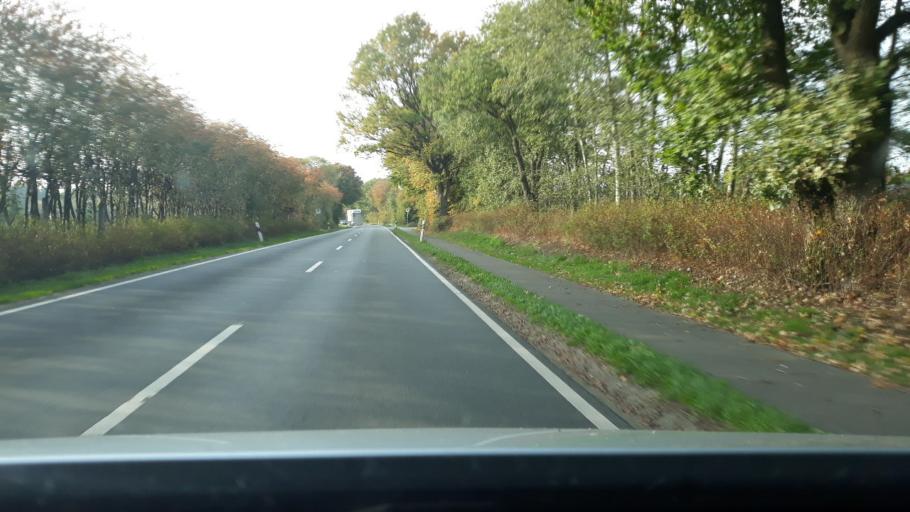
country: DE
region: Schleswig-Holstein
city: Owschlag
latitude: 54.3974
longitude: 9.5592
